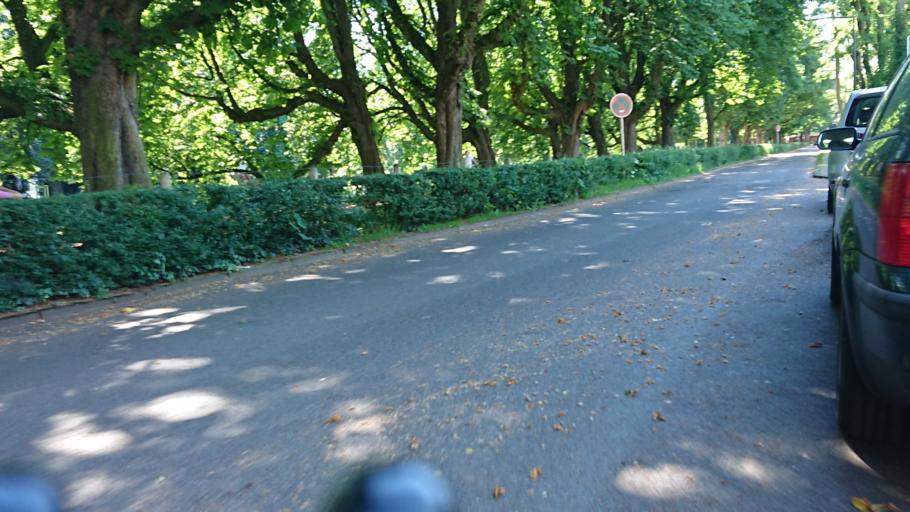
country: DE
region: North Rhine-Westphalia
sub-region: Regierungsbezirk Koln
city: Neuehrenfeld
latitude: 50.9355
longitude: 6.9219
